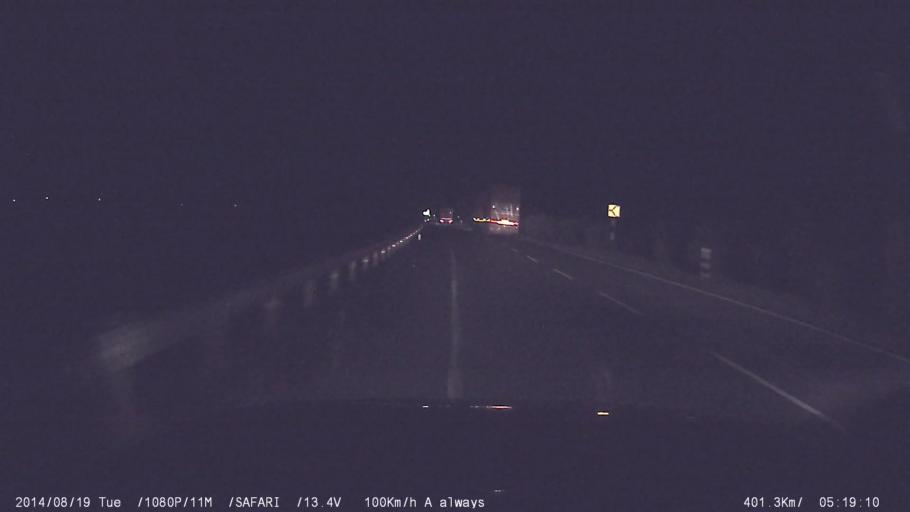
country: IN
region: Tamil Nadu
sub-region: Salem
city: Konganapuram
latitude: 11.5315
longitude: 77.9550
